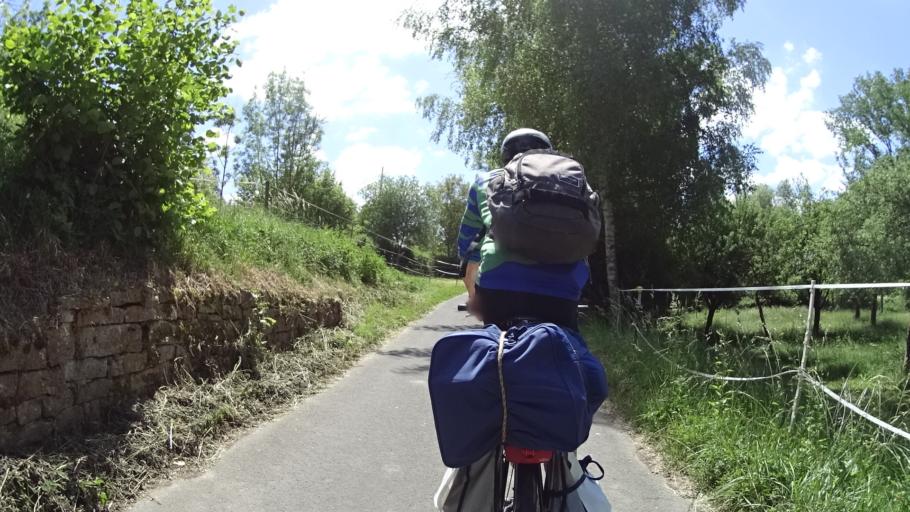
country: DE
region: Bavaria
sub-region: Regierungsbezirk Unterfranken
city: Bieberehren
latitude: 49.5051
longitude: 10.0190
